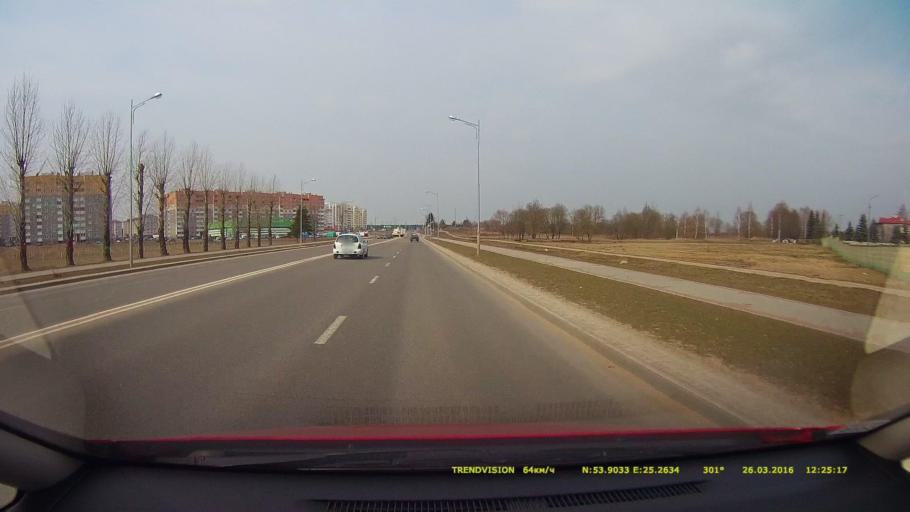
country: BY
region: Grodnenskaya
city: Lida
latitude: 53.9034
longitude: 25.2632
